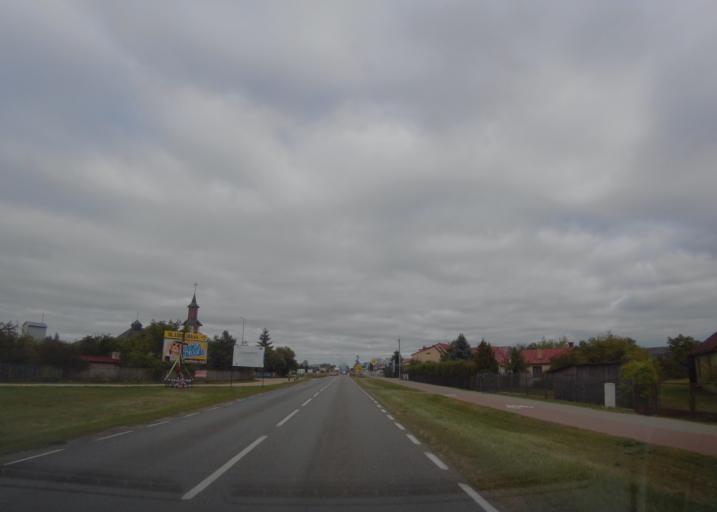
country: PL
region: Lublin Voivodeship
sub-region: Powiat wlodawski
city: Wlodawa
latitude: 51.5443
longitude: 23.5413
